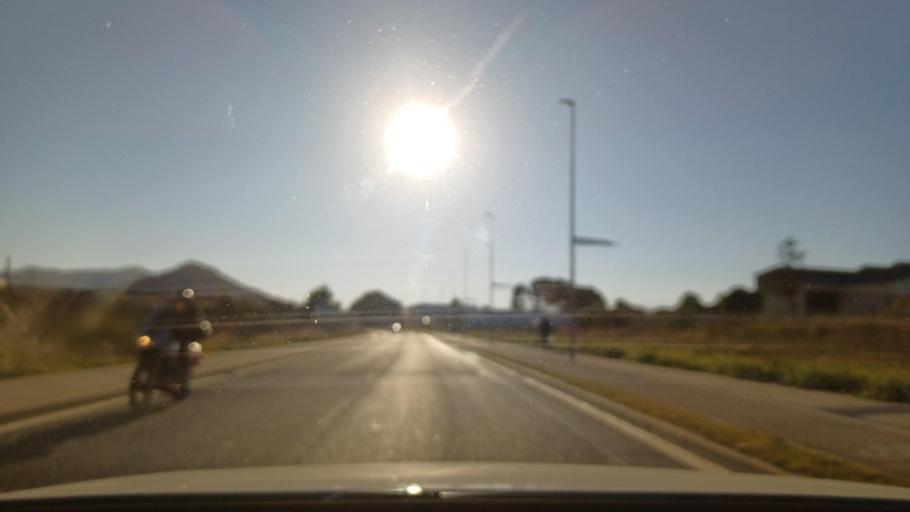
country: ES
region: Catalonia
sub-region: Provincia de Tarragona
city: Amposta
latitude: 40.7051
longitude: 0.5693
